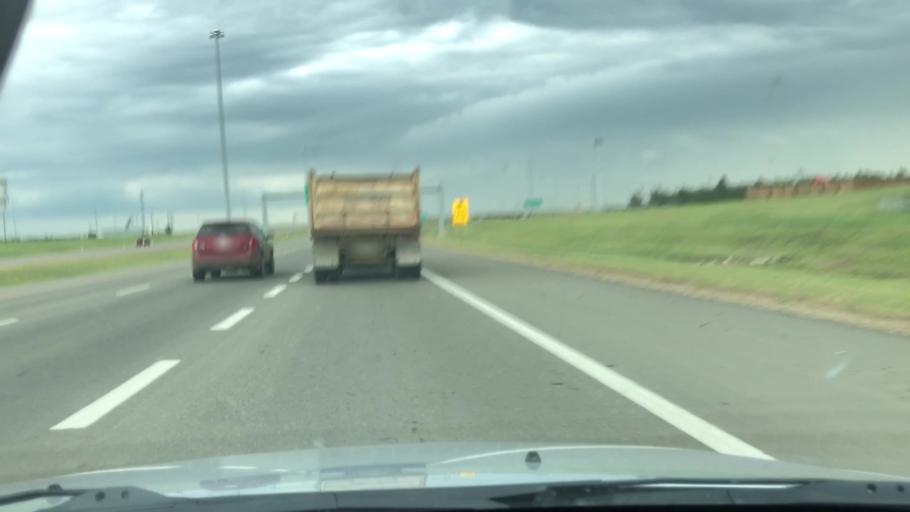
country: CA
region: Alberta
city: Sherwood Park
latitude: 53.5149
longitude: -113.3569
